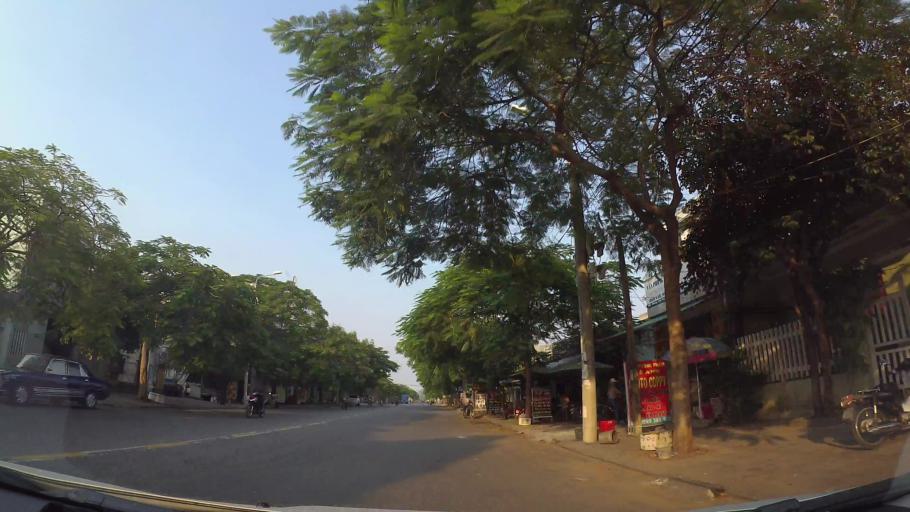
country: VN
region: Da Nang
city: Ngu Hanh Son
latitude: 15.9847
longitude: 108.2392
